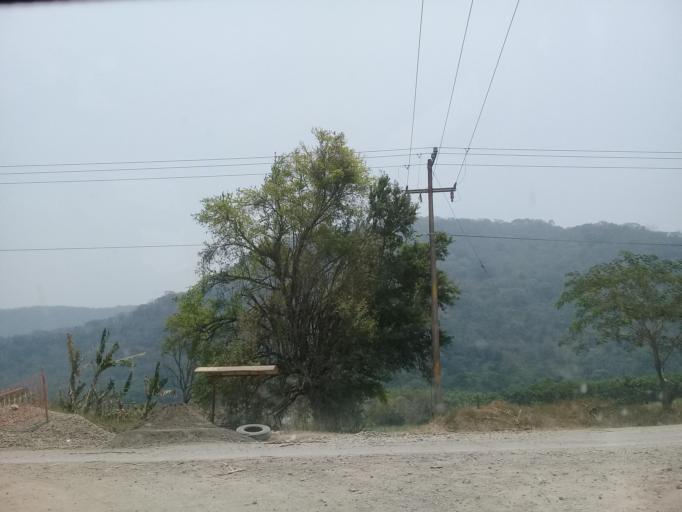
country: MX
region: Veracruz
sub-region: Tezonapa
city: Laguna Chica (Pueblo Nuevo)
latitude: 18.5682
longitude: -96.7204
